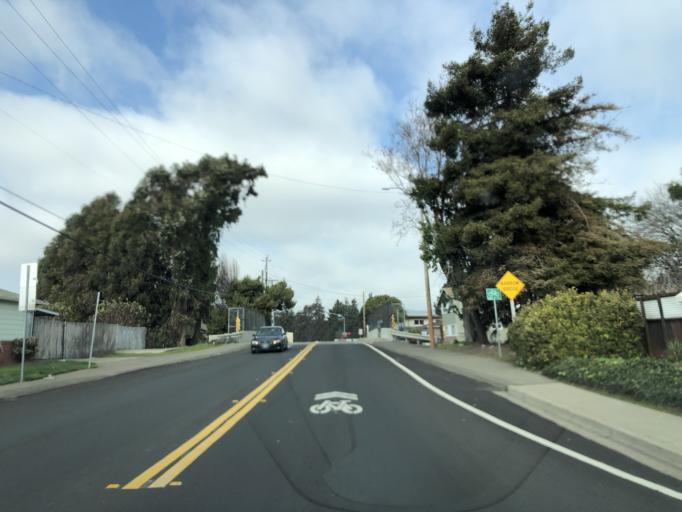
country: US
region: California
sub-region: Alameda County
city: San Lorenzo
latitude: 37.6852
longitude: -122.1249
